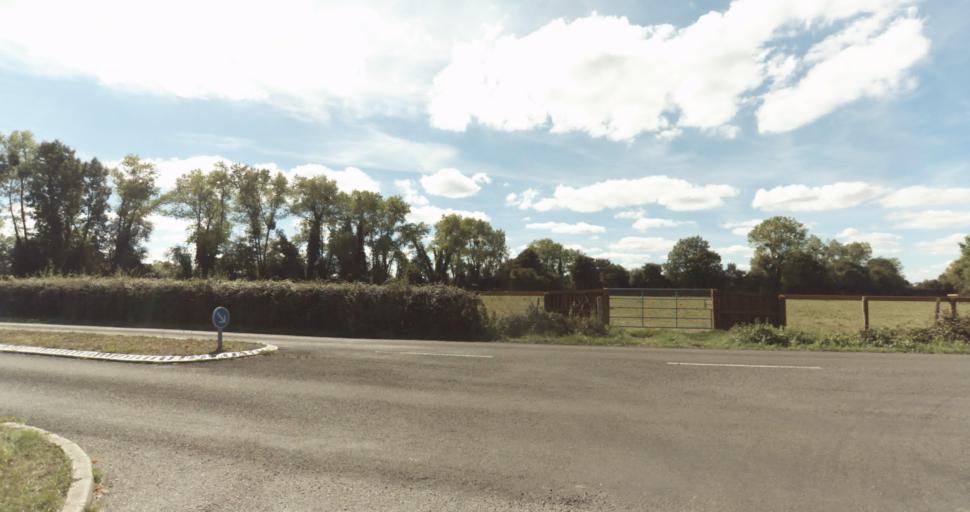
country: FR
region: Lower Normandy
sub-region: Departement de l'Orne
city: Vimoutiers
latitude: 48.9290
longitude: 0.2456
